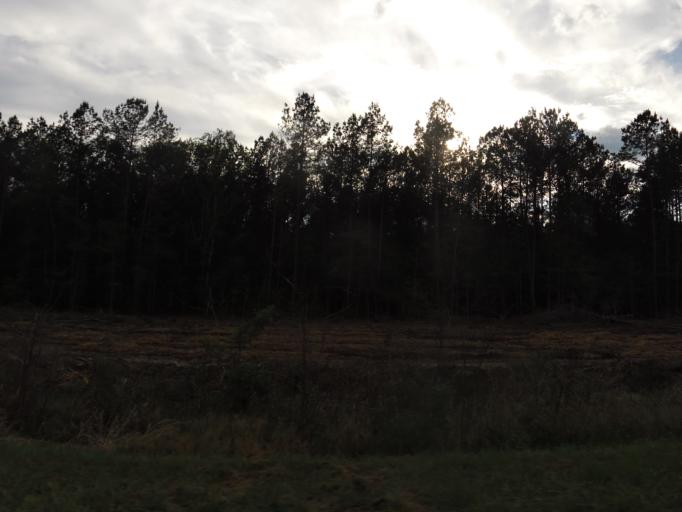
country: US
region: South Carolina
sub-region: Jasper County
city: Ridgeland
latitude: 32.4242
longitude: -81.1025
